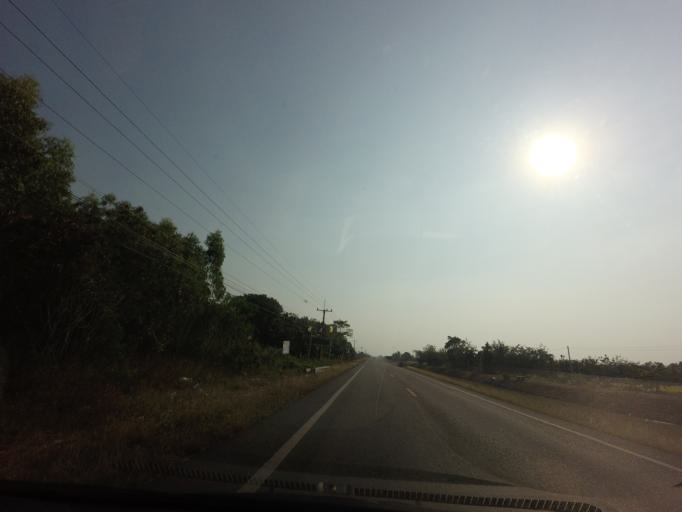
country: TH
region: Chachoengsao
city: Khlong Khuean
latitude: 13.7862
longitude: 101.1752
